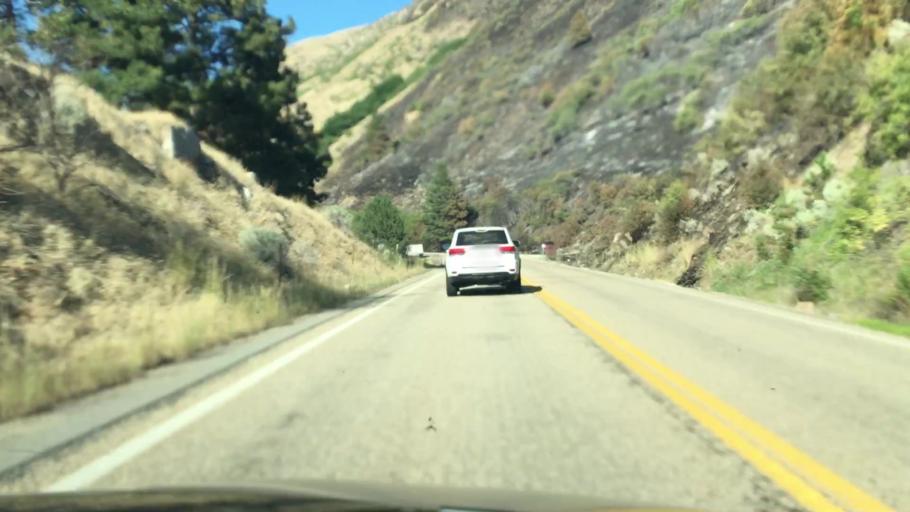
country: US
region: Idaho
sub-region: Gem County
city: Emmett
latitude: 44.0142
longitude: -116.1568
